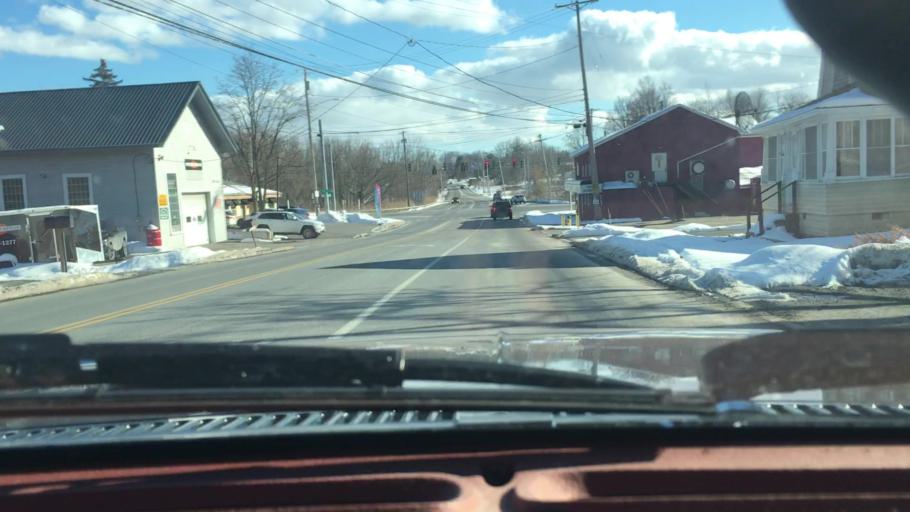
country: US
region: New York
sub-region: Onondaga County
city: Liverpool
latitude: 43.1873
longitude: -76.2171
